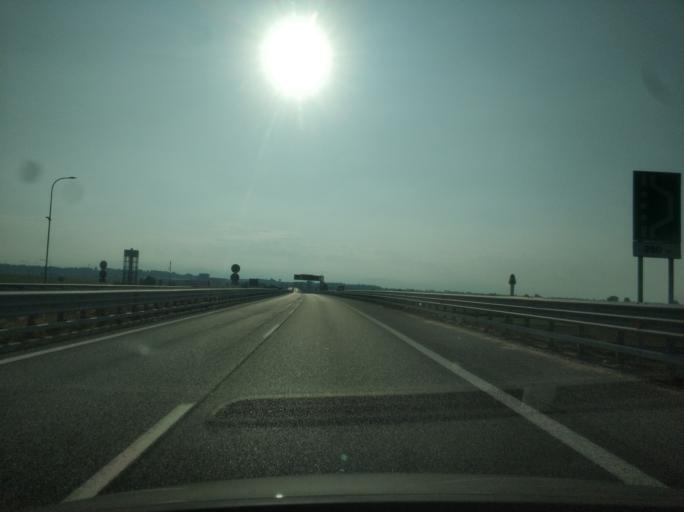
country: IT
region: Piedmont
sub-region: Provincia di Cuneo
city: Roreto
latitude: 44.6650
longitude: 7.8037
